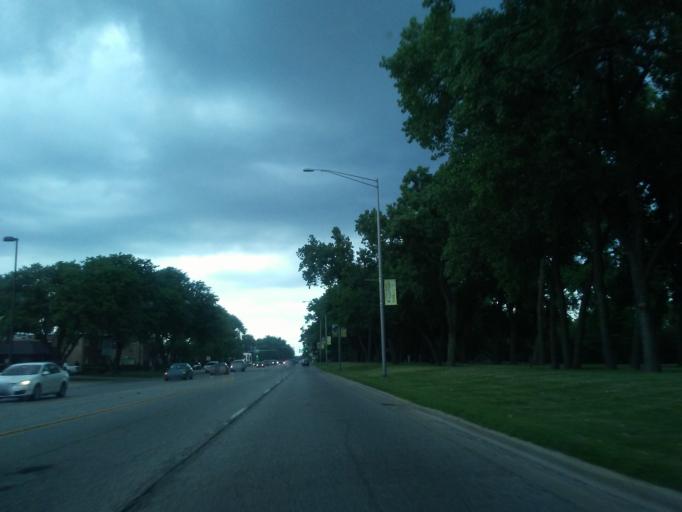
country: US
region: Illinois
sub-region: Cook County
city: Skokie
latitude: 42.0309
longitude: -87.7109
